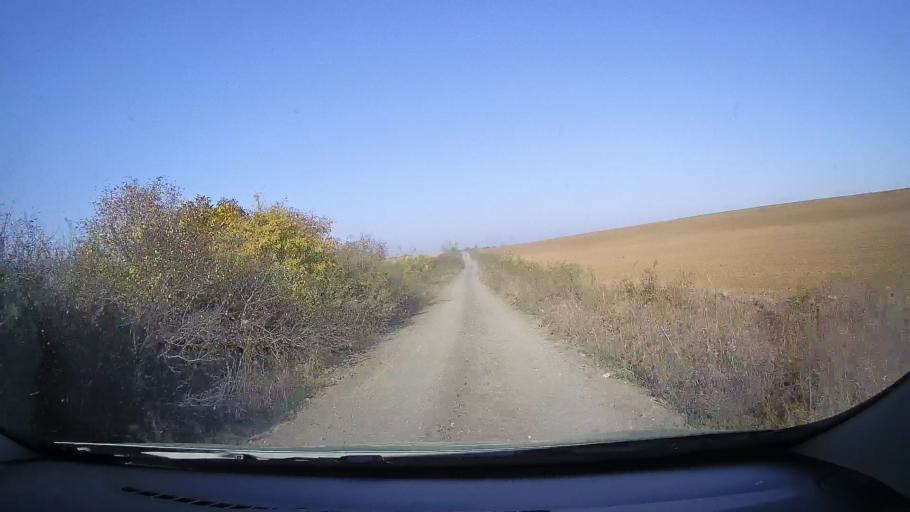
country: RO
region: Satu Mare
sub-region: Comuna Sauca
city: Sauca
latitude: 47.4802
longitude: 22.4701
